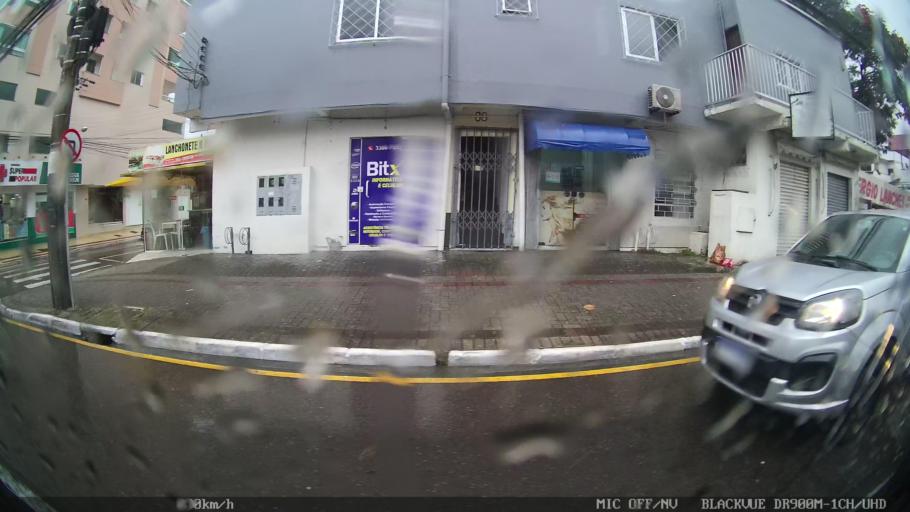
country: BR
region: Santa Catarina
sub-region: Balneario Camboriu
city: Balneario Camboriu
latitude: -26.9766
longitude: -48.6463
